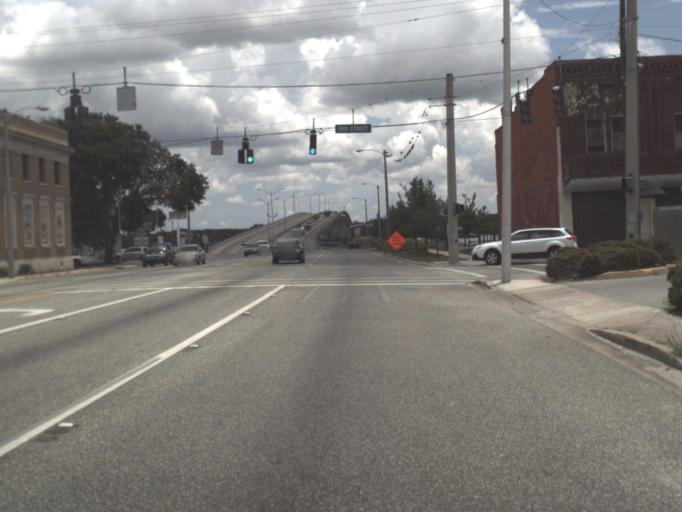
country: US
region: Florida
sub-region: Putnam County
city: Palatka
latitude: 29.6472
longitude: -81.6302
